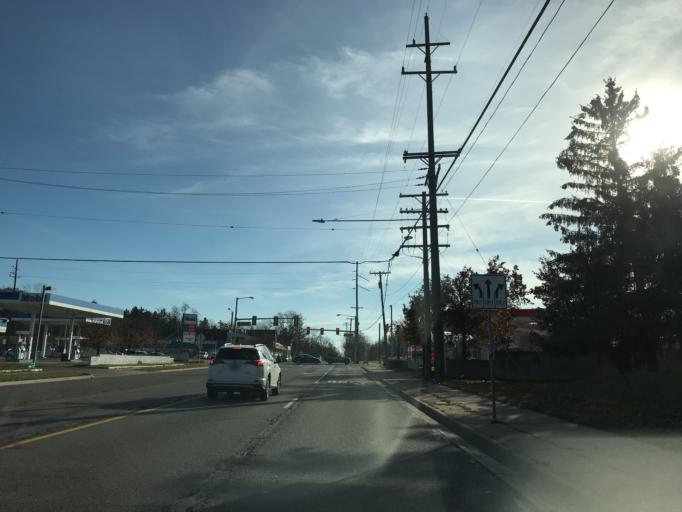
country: US
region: Michigan
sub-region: Washtenaw County
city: Ann Arbor
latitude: 42.2461
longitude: -83.7002
